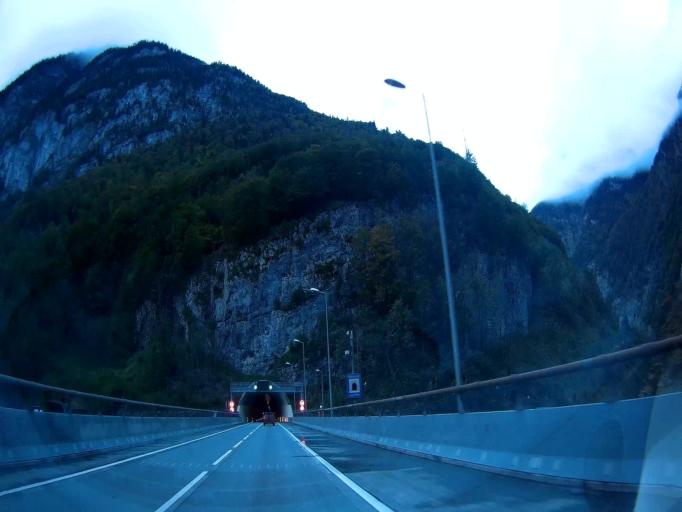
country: AT
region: Salzburg
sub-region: Politischer Bezirk Hallein
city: Golling an der Salzach
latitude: 47.5666
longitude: 13.1704
